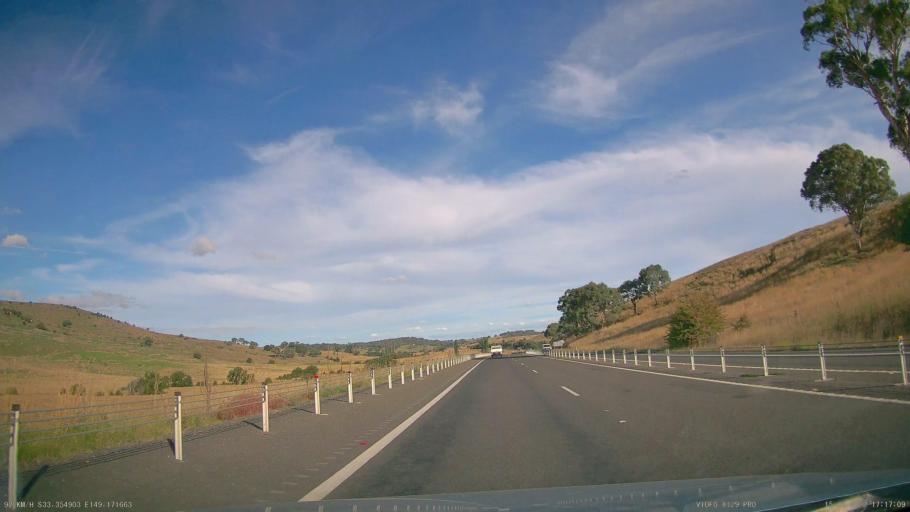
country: AU
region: New South Wales
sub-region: Blayney
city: Millthorpe
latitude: -33.3552
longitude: 149.1718
